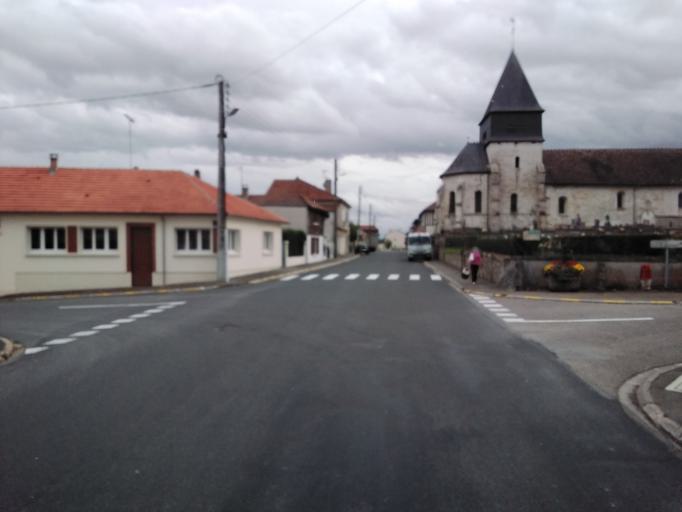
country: FR
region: Champagne-Ardenne
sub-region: Departement de la Marne
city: Frignicourt
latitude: 48.6724
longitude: 4.5828
